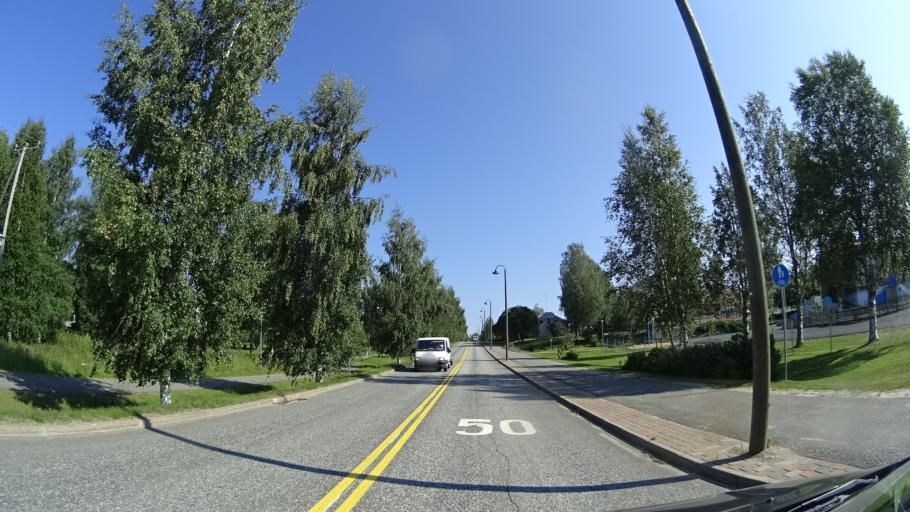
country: FI
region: North Karelia
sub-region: Joensuu
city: Juuka
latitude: 63.2382
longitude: 29.2492
